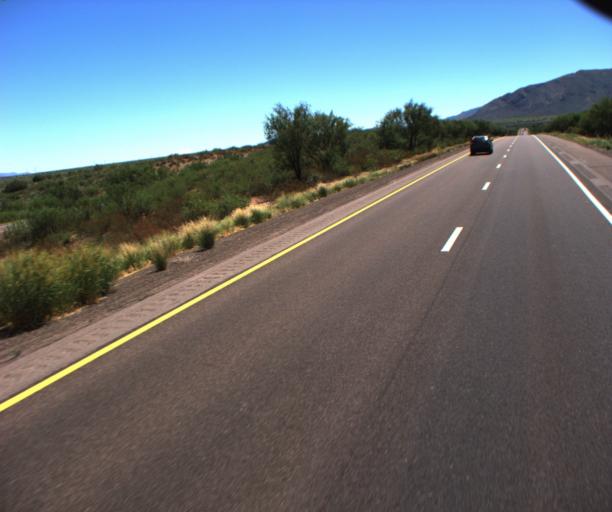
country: US
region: Arizona
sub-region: Gila County
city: Payson
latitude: 34.0788
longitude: -111.3571
